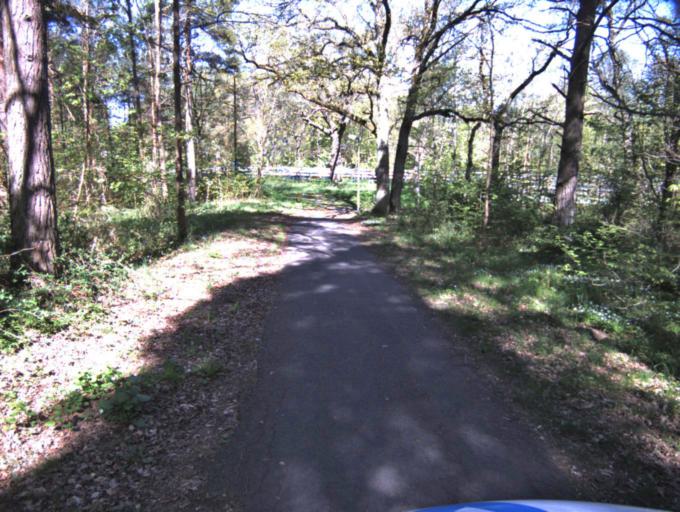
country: SE
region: Skane
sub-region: Kristianstads Kommun
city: Onnestad
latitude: 55.9290
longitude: 13.9765
